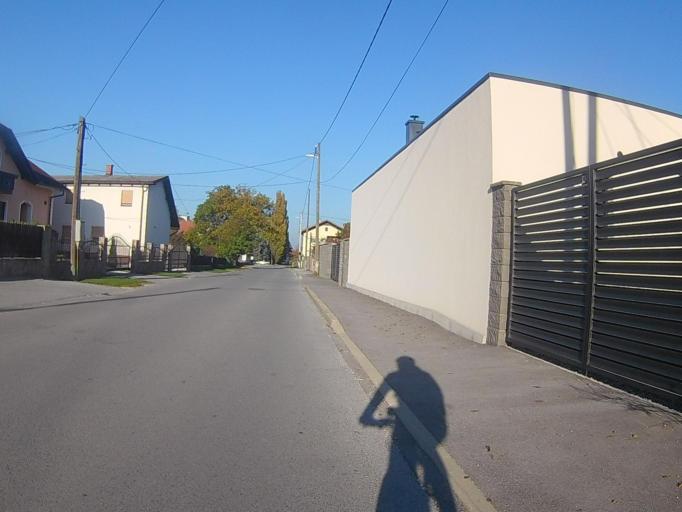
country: SI
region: Hoce-Slivnica
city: Spodnje Hoce
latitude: 46.4984
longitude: 15.6397
